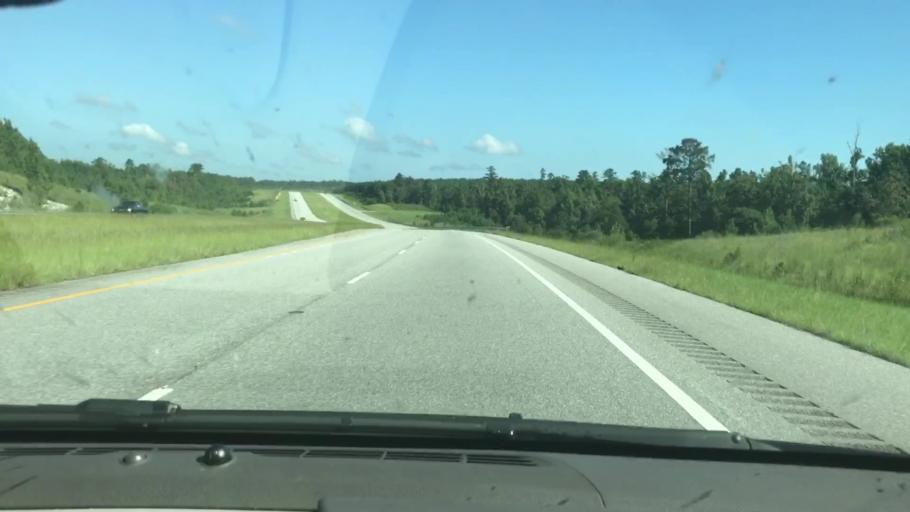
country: US
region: Alabama
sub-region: Barbour County
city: Eufaula
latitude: 32.1133
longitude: -85.1501
